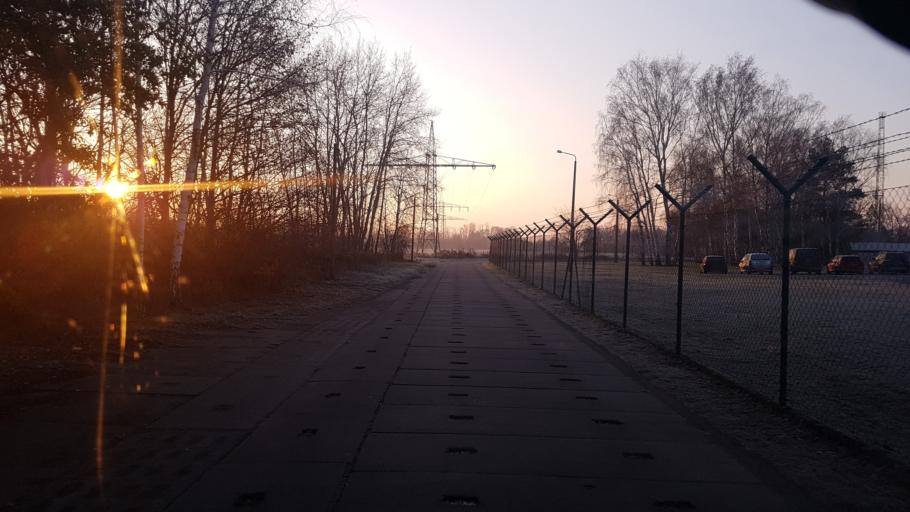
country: DE
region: Brandenburg
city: Lauchhammer
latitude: 51.4810
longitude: 13.7218
